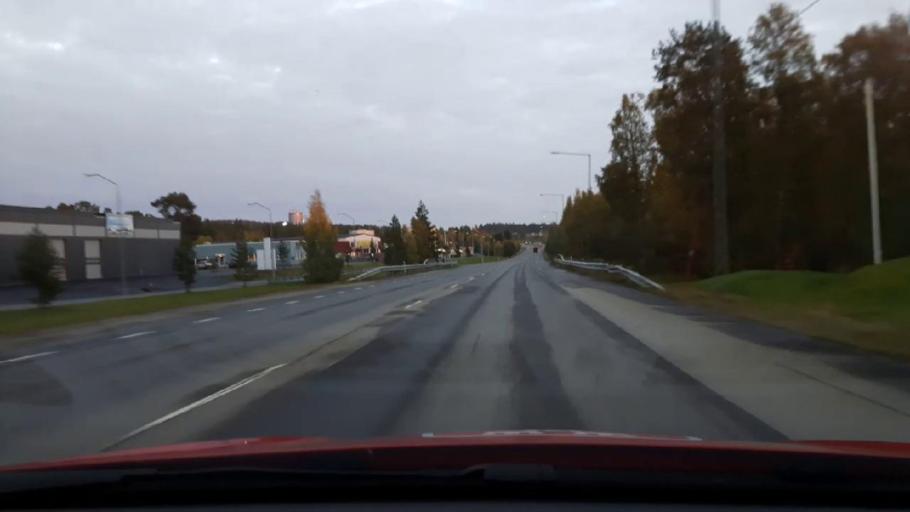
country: SE
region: Jaemtland
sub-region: OEstersunds Kommun
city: Ostersund
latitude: 63.2053
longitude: 14.6401
